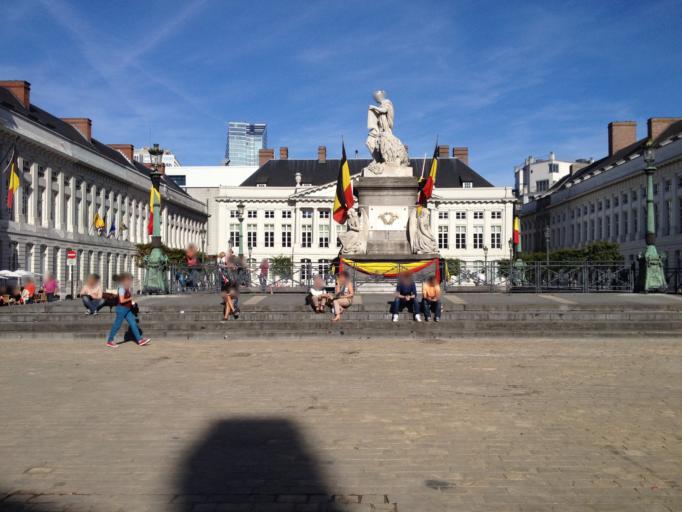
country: BE
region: Brussels Capital
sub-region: Bruxelles-Capitale
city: Brussels
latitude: 50.8515
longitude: 4.3562
